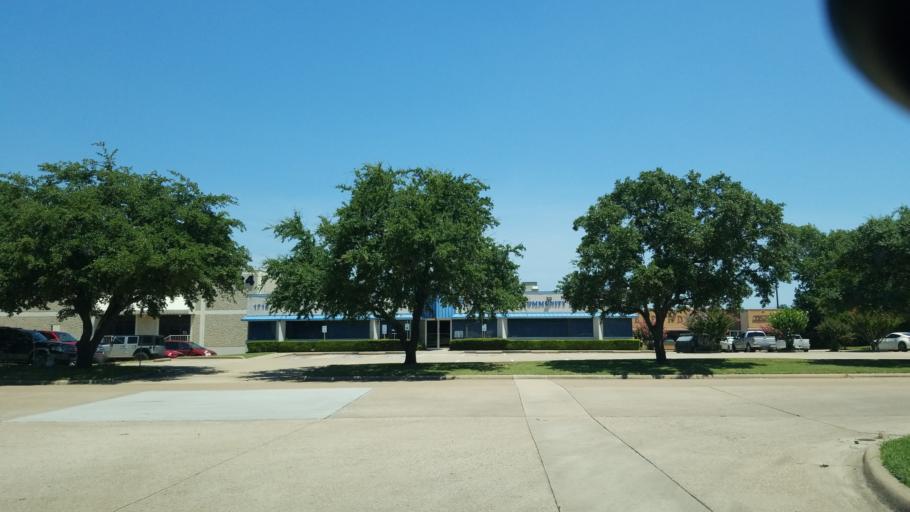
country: US
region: Texas
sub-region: Dallas County
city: Farmers Branch
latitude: 32.9223
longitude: -96.9272
